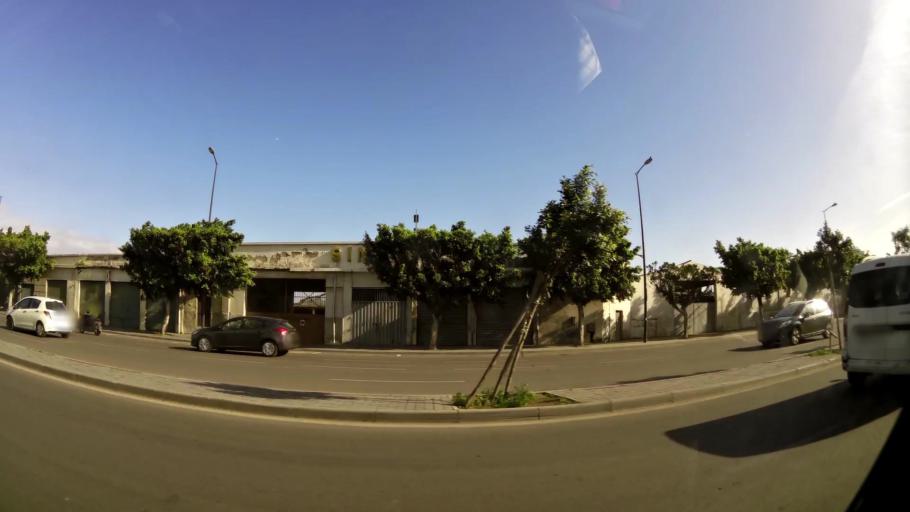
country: MA
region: Grand Casablanca
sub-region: Casablanca
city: Casablanca
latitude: 33.5961
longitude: -7.5998
